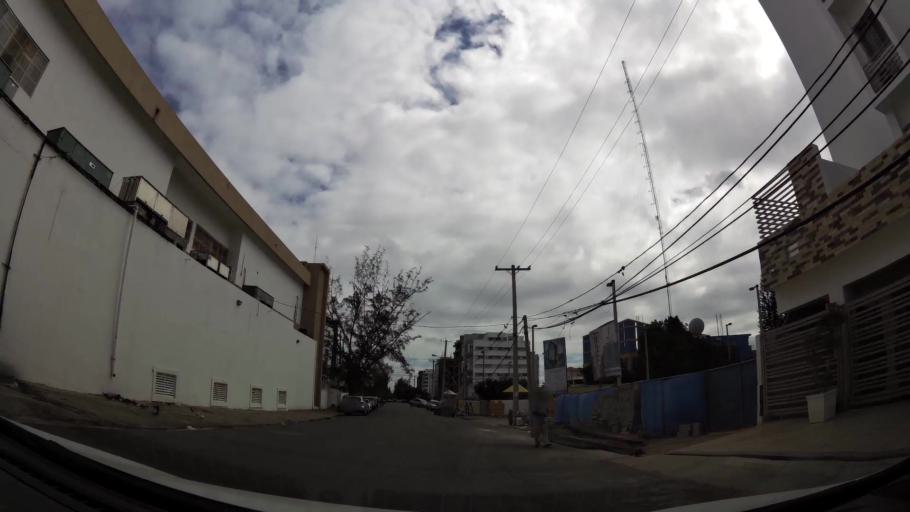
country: DO
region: Nacional
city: Bella Vista
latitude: 18.4465
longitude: -69.9573
